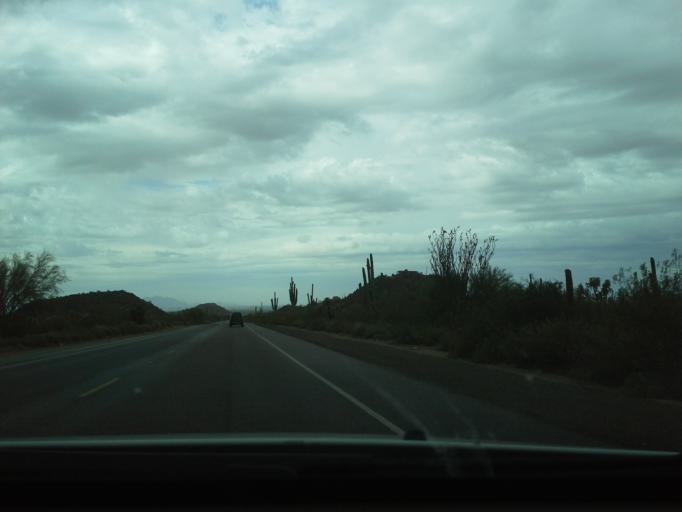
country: US
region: Arizona
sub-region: Pinal County
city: Apache Junction
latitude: 33.4745
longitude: -111.6272
